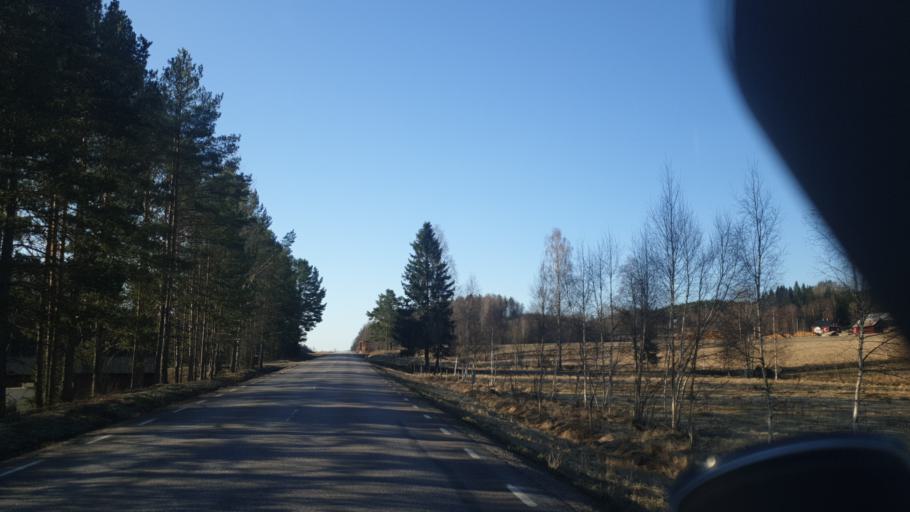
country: SE
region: Vaermland
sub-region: Arvika Kommun
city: Arvika
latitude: 59.7420
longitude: 12.6400
